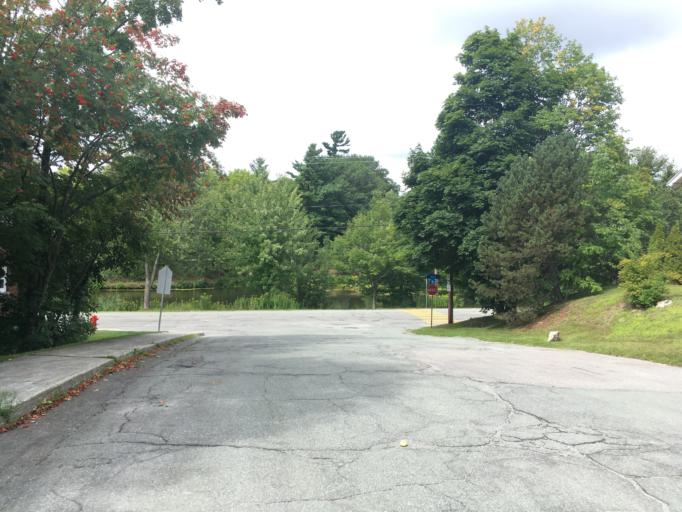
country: CA
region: Quebec
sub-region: Estrie
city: Sherbrooke
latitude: 45.4016
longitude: -71.9073
